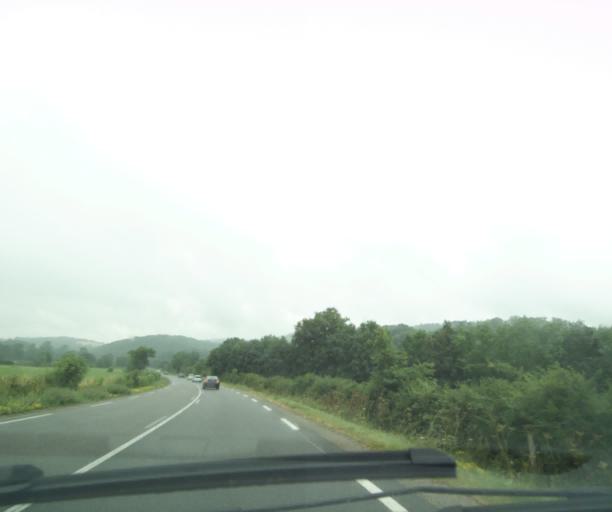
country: FR
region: Midi-Pyrenees
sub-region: Departement de l'Aveyron
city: Bozouls
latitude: 44.3998
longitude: 2.7450
